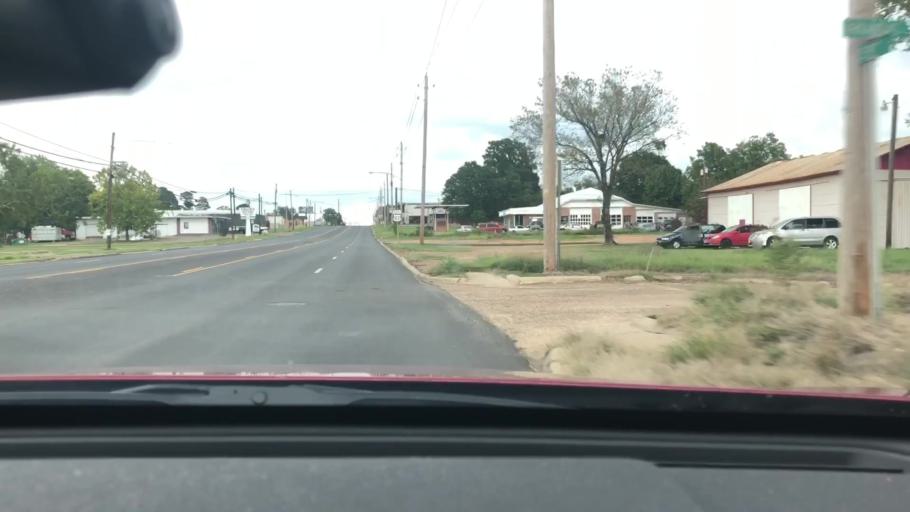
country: US
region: Arkansas
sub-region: Miller County
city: Texarkana
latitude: 33.4307
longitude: -94.0202
